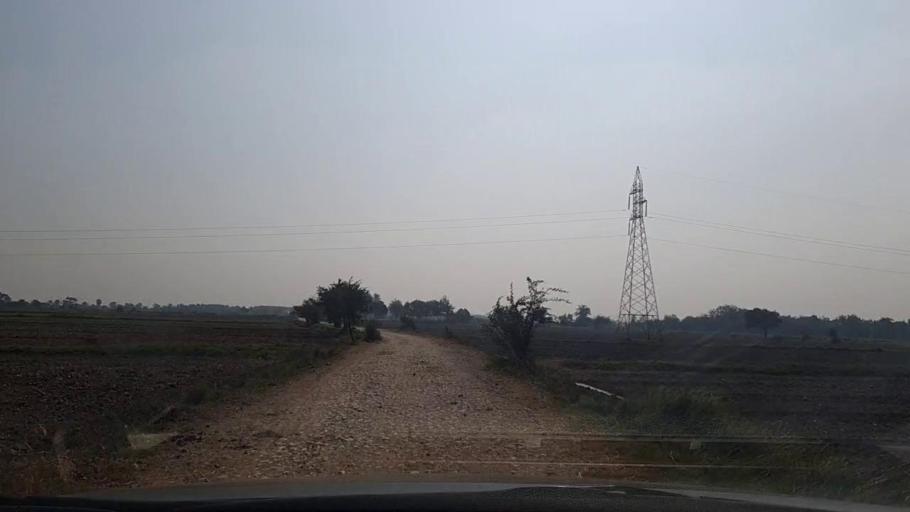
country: PK
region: Sindh
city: Mirpur Sakro
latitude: 24.5681
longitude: 67.7765
